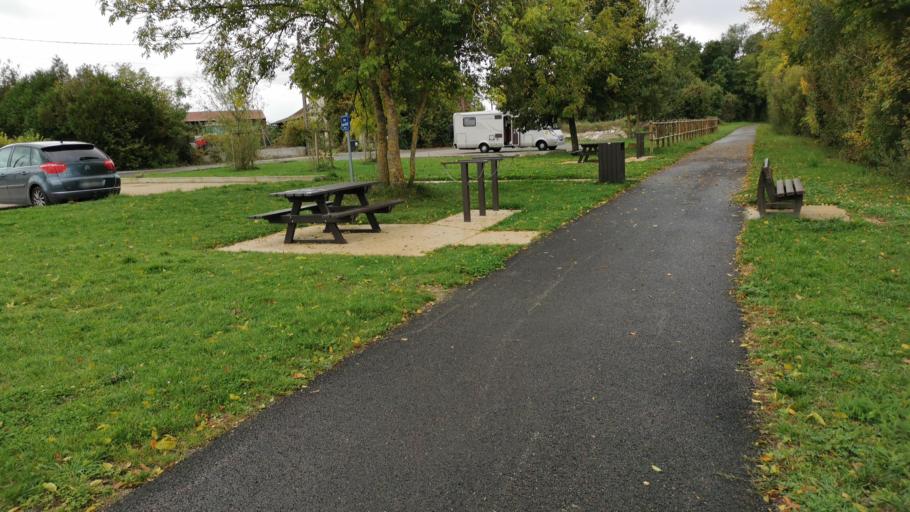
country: FR
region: Champagne-Ardenne
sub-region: Departement de l'Aube
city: Romilly-sur-Seine
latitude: 48.5556
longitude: 3.7118
